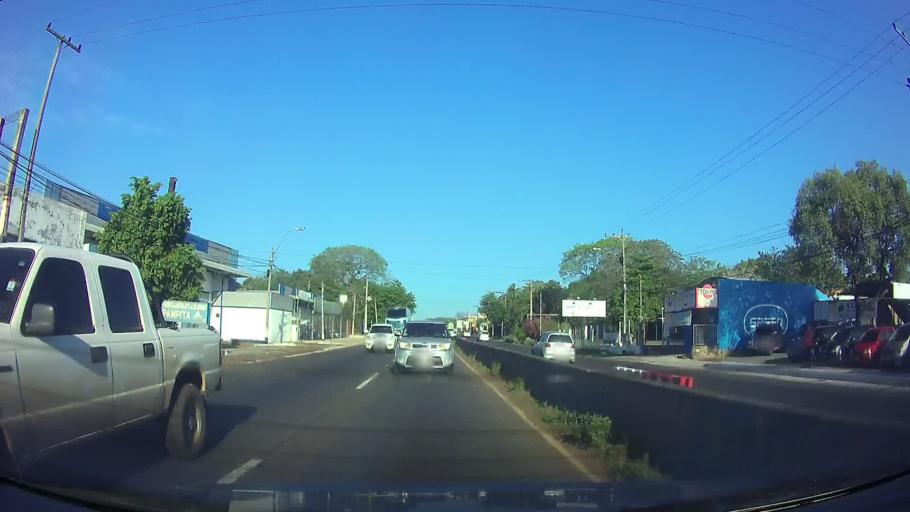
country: PY
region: Central
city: San Lorenzo
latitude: -25.3459
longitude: -57.4776
